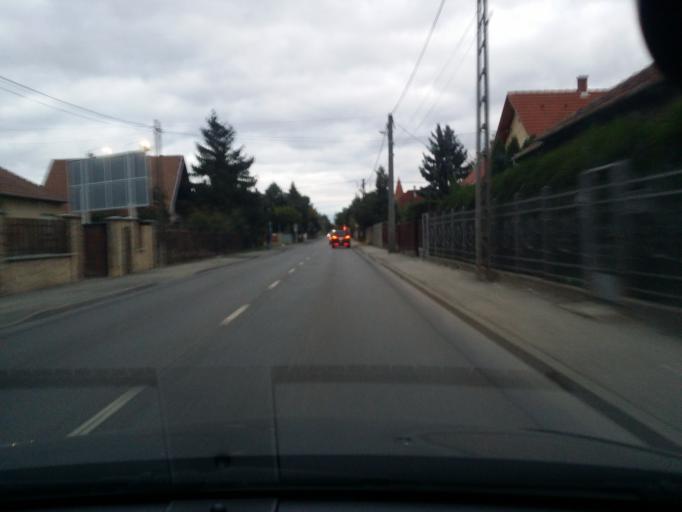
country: HU
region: Budapest
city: Budapest XVI. keruelet
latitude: 47.5259
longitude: 19.1556
